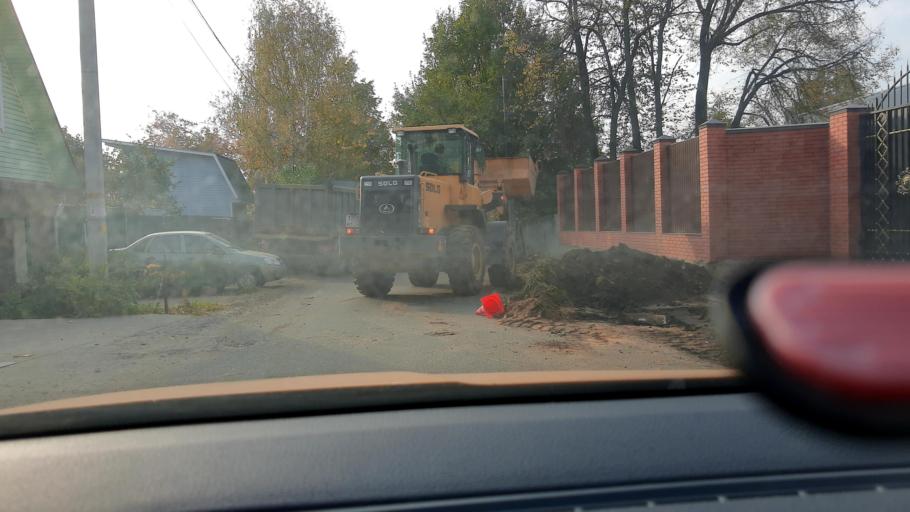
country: RU
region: Moskovskaya
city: Odintsovo
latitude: 55.6938
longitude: 37.3200
